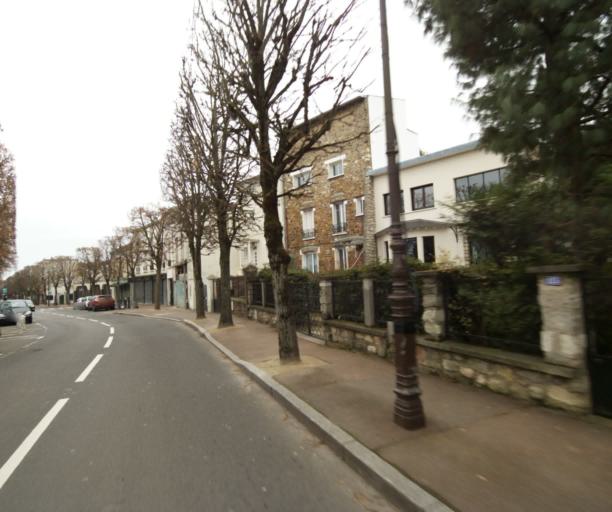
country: FR
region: Ile-de-France
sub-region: Departement des Hauts-de-Seine
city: Saint-Cloud
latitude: 48.8481
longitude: 2.2041
